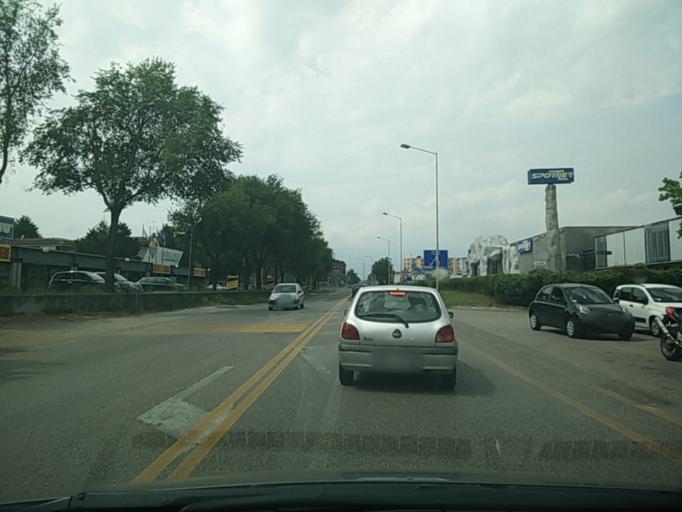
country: IT
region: Friuli Venezia Giulia
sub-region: Provincia di Pordenone
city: Pordenone
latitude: 45.9618
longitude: 12.6762
